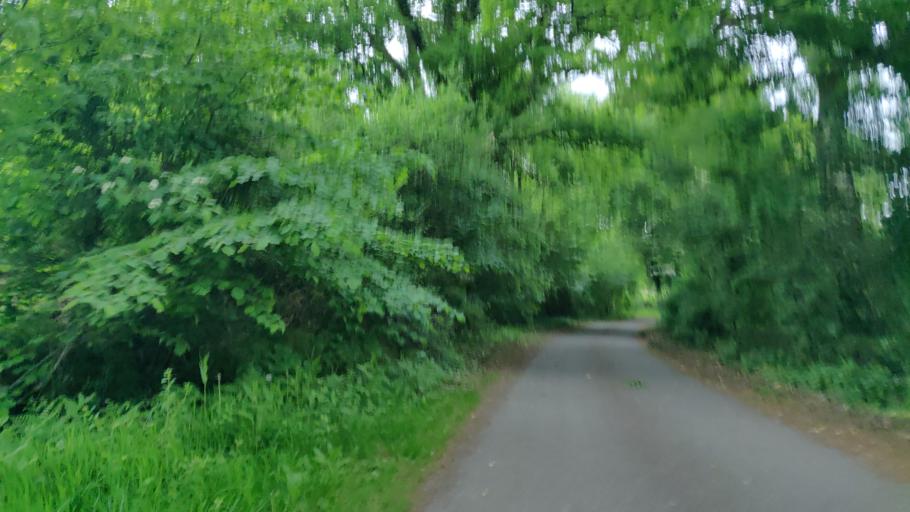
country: GB
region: England
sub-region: West Sussex
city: Southwater
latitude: 51.0209
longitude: -0.3310
